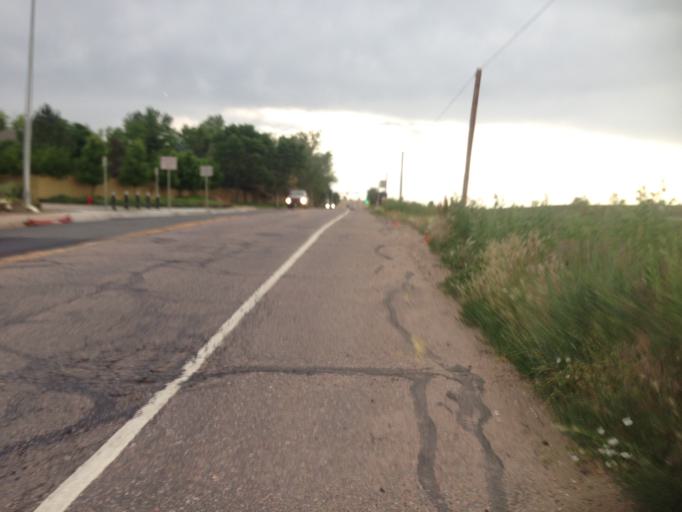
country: US
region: Colorado
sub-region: Boulder County
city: Superior
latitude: 39.9411
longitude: -105.1470
